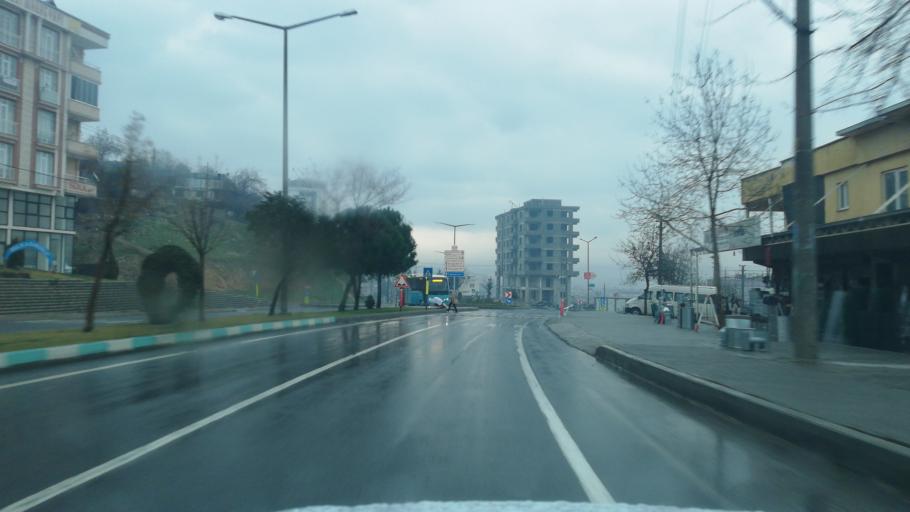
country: TR
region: Kahramanmaras
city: Kahramanmaras
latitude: 37.5821
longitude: 36.9559
